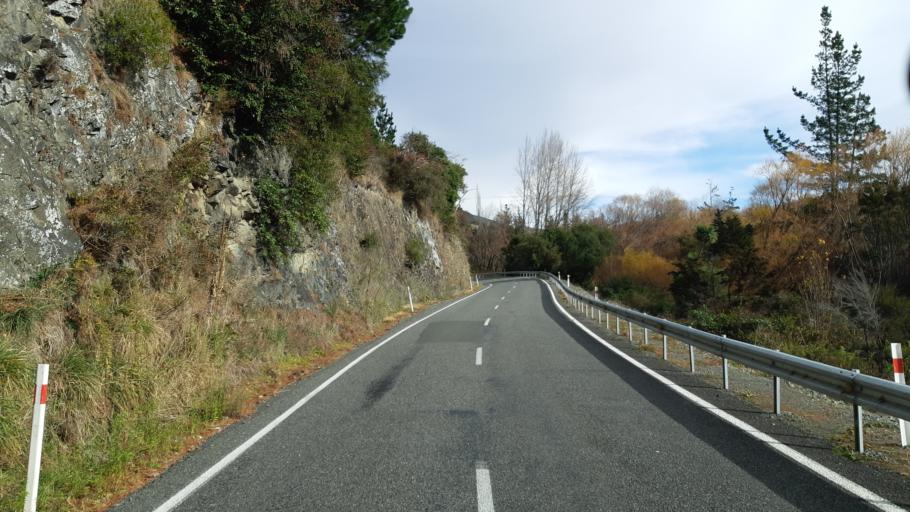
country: NZ
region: Tasman
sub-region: Tasman District
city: Wakefield
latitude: -41.7157
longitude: 173.1087
